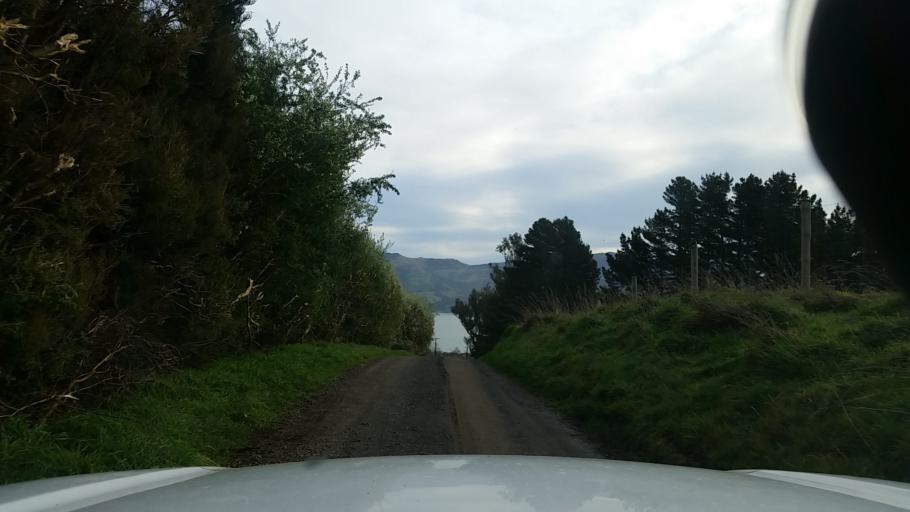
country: NZ
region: Canterbury
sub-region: Christchurch City
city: Christchurch
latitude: -43.8088
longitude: 172.9858
